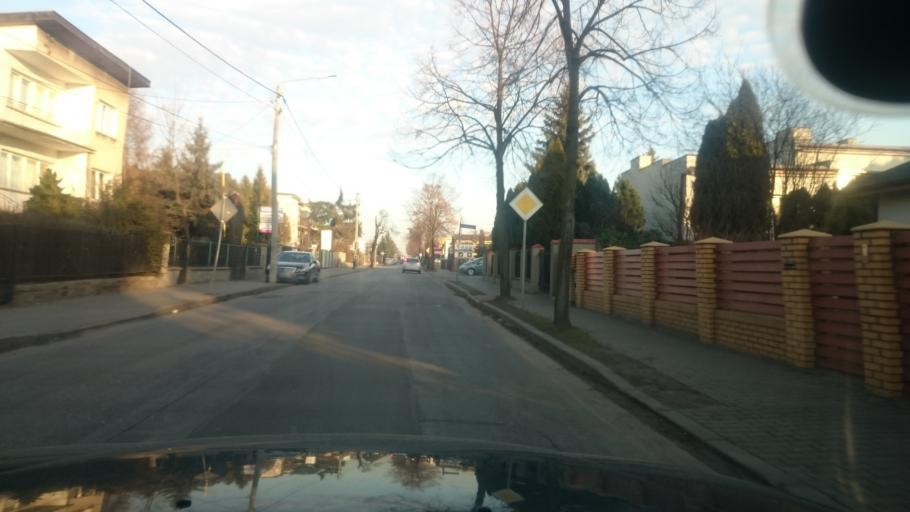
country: PL
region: Greater Poland Voivodeship
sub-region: Powiat ostrowski
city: Ostrow Wielkopolski
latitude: 51.6475
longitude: 17.8264
